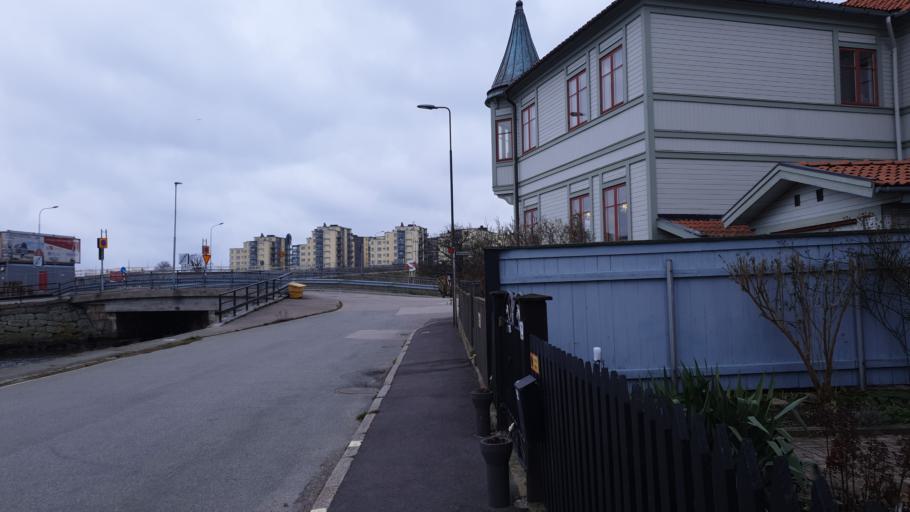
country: SE
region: Blekinge
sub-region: Karlskrona Kommun
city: Karlskrona
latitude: 56.1642
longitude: 15.5730
